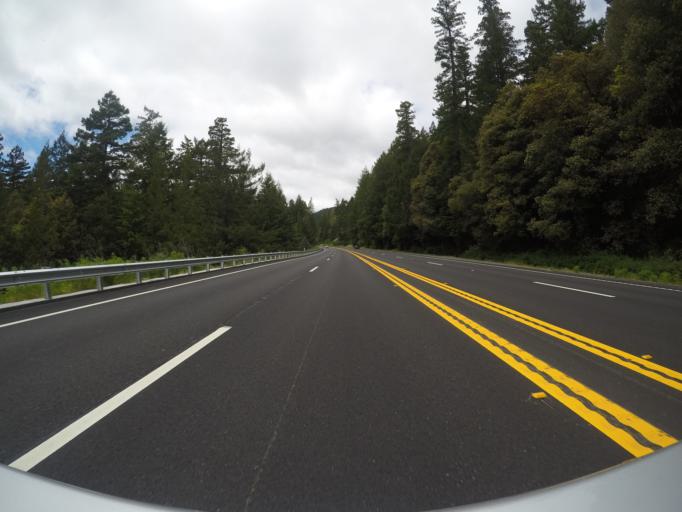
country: US
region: California
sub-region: Humboldt County
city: Redway
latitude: 40.3325
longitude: -123.9281
